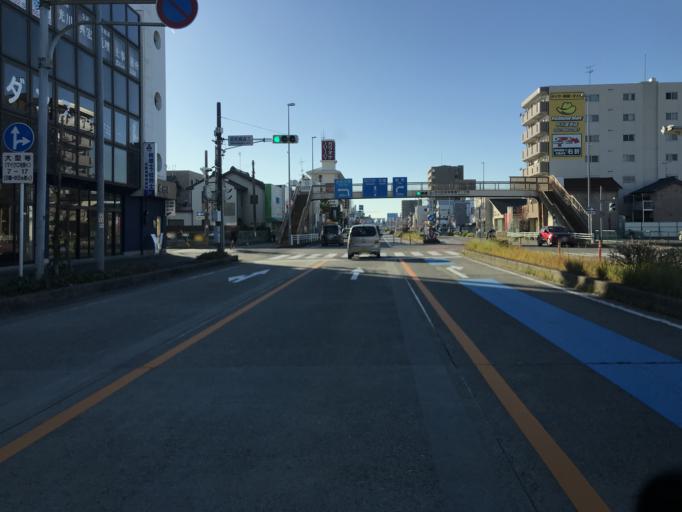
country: JP
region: Aichi
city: Nagoya-shi
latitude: 35.1251
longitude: 136.8738
